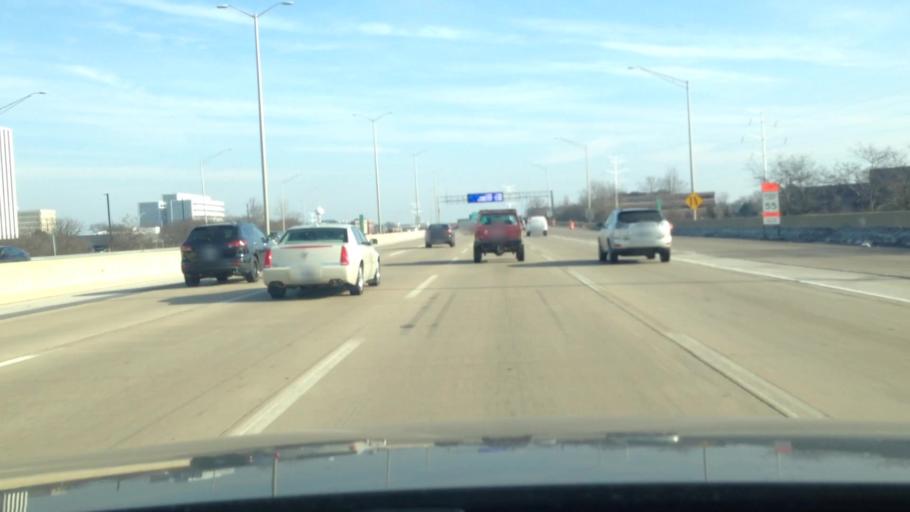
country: US
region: Illinois
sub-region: DuPage County
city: Oakbrook Terrace
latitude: 41.8446
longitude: -87.9527
